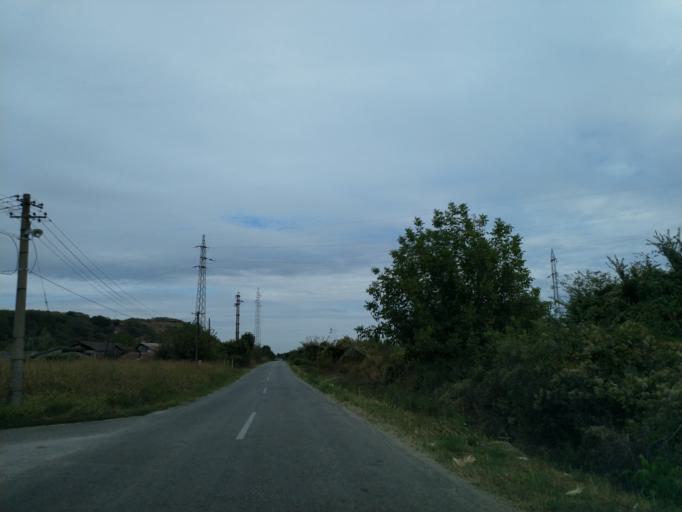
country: RS
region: Central Serbia
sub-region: Pomoravski Okrug
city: Cuprija
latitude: 43.9442
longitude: 21.3197
